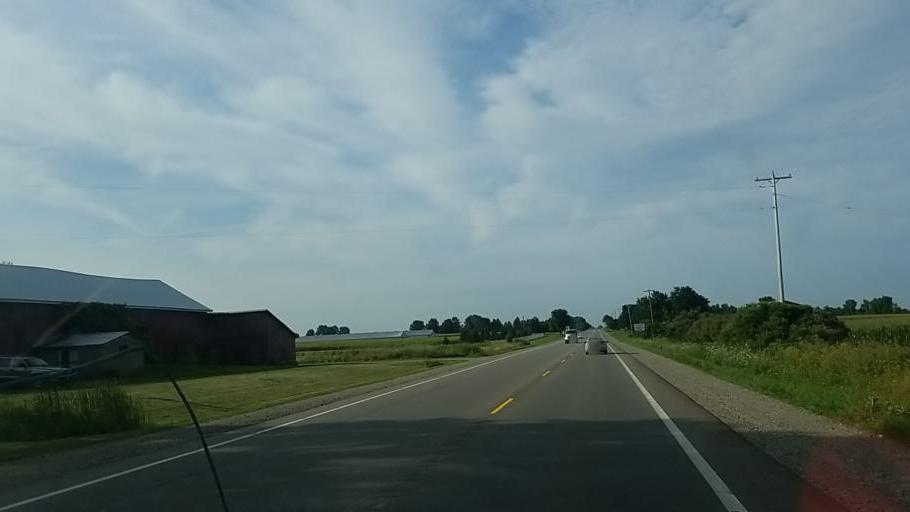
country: US
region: Michigan
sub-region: Ionia County
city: Ionia
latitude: 42.8964
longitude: -85.0750
